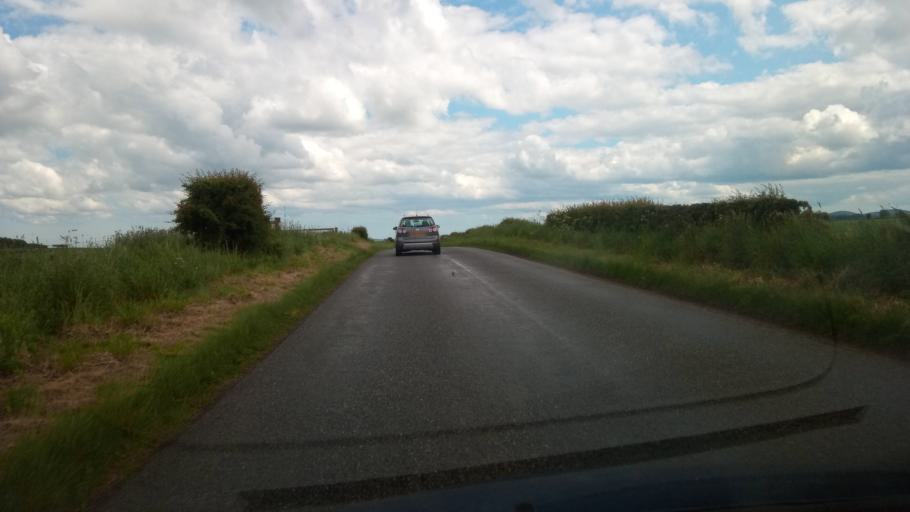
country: GB
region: Scotland
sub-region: The Scottish Borders
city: Kelso
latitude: 55.5974
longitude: -2.3494
